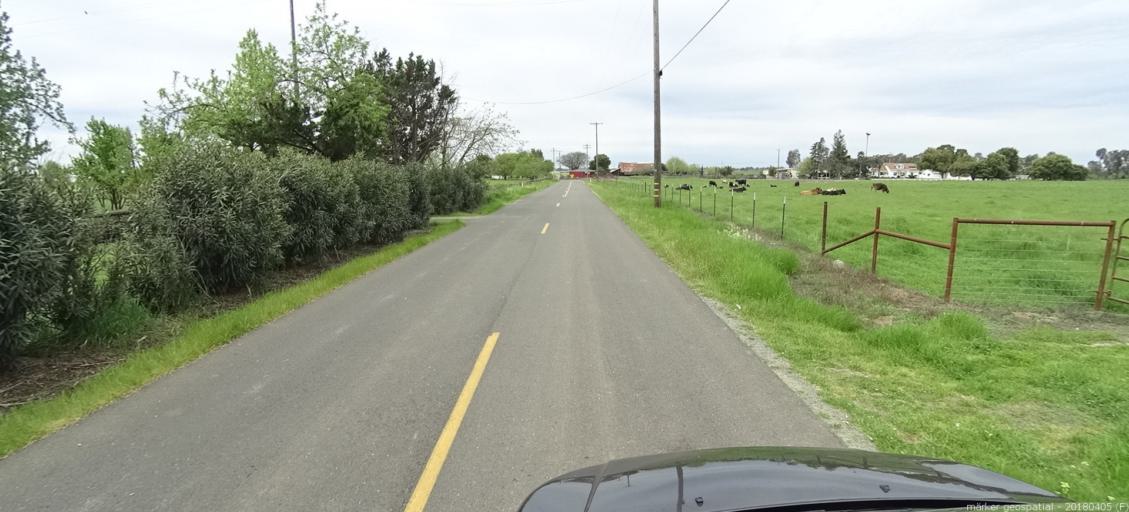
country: US
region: California
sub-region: Sacramento County
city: Galt
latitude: 38.2836
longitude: -121.3351
